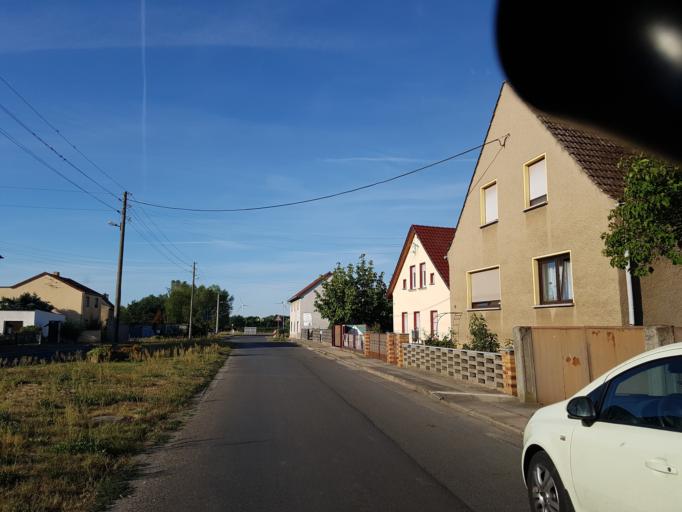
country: DE
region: Brandenburg
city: Elsterwerda
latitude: 51.4700
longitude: 13.5001
